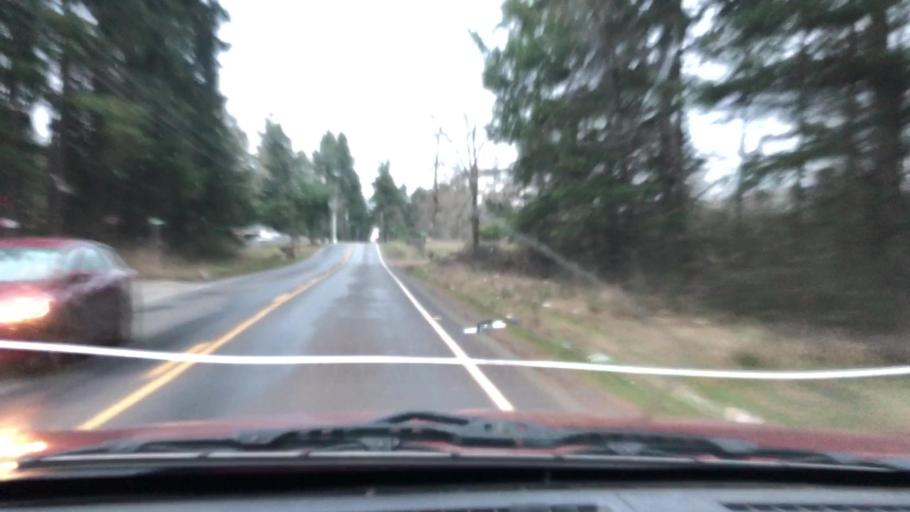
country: US
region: Washington
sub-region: Pierce County
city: Elk Plain
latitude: 47.0601
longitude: -122.4003
